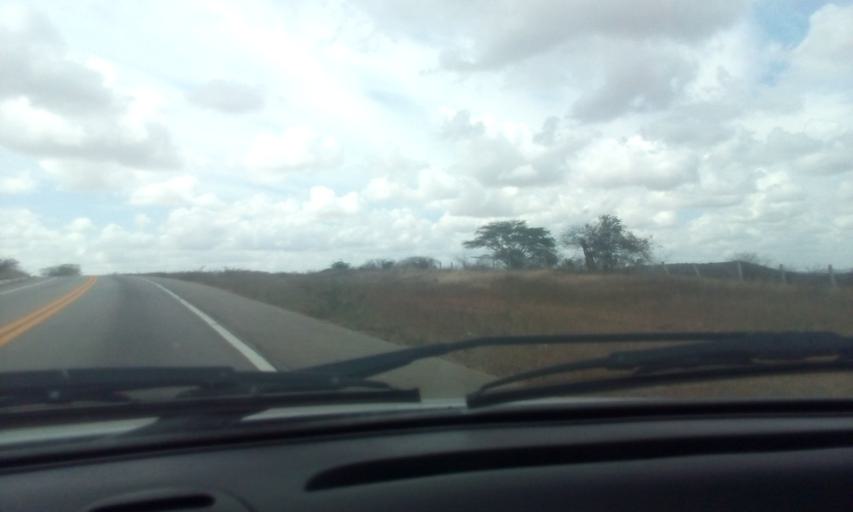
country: BR
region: Rio Grande do Norte
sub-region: Tangara
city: Tangara
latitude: -6.1144
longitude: -35.7169
